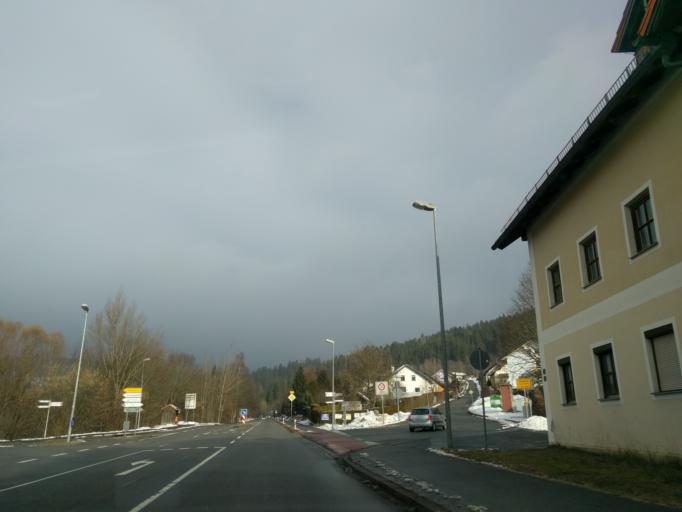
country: DE
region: Bavaria
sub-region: Lower Bavaria
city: Zwiesel
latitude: 49.0354
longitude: 13.2337
